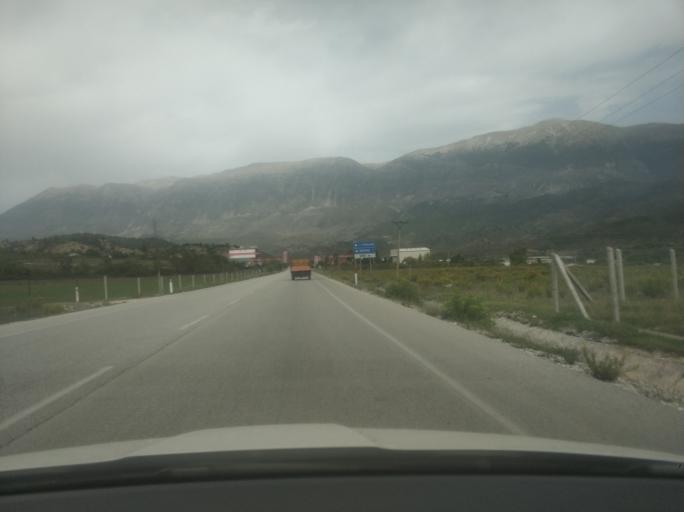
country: AL
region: Gjirokaster
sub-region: Rrethi i Gjirokastres
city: Picar
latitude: 40.1849
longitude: 20.0772
